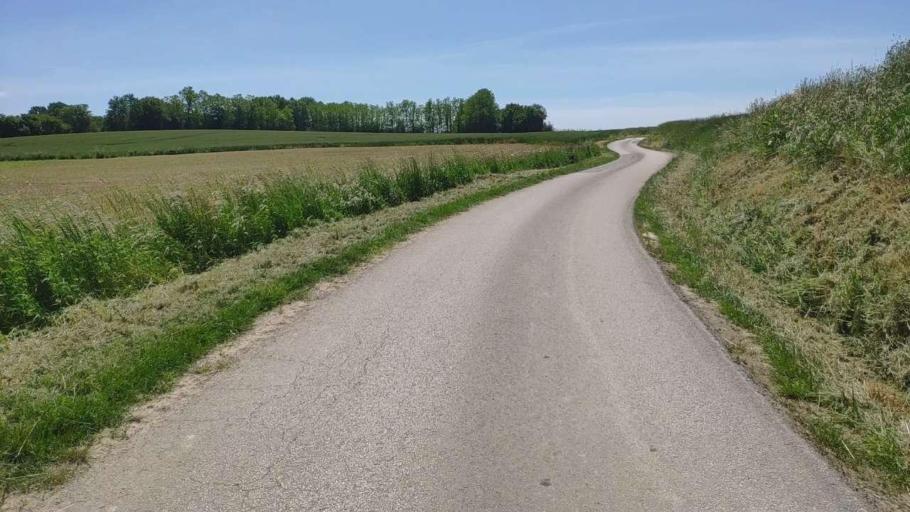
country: FR
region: Franche-Comte
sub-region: Departement du Jura
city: Bletterans
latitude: 46.7584
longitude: 5.4062
